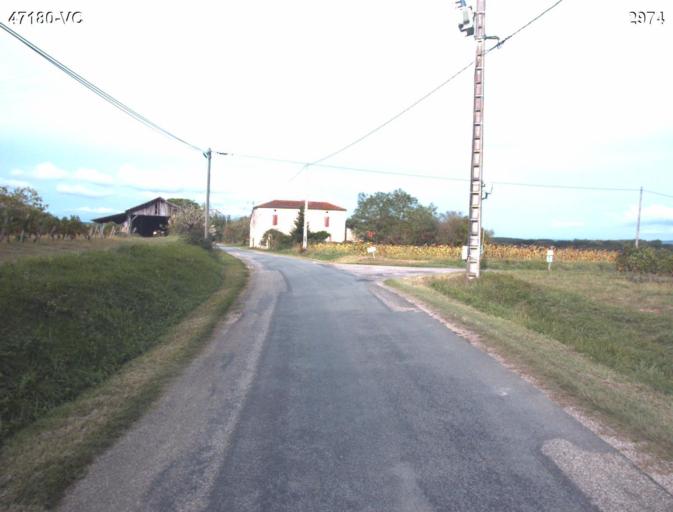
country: FR
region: Aquitaine
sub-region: Departement du Lot-et-Garonne
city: Sainte-Colombe-en-Bruilhois
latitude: 44.1696
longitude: 0.4516
